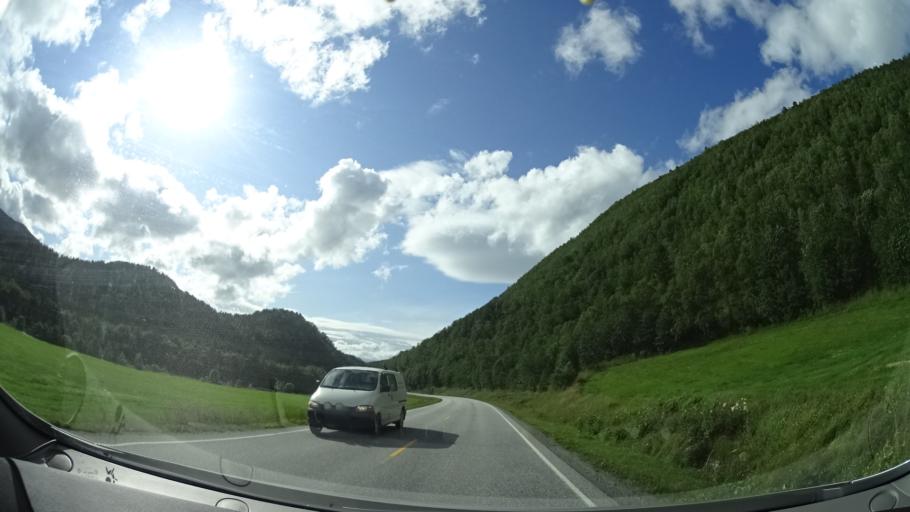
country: NO
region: Sor-Trondelag
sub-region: Hemne
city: Kyrksaeterora
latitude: 63.2103
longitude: 9.1586
